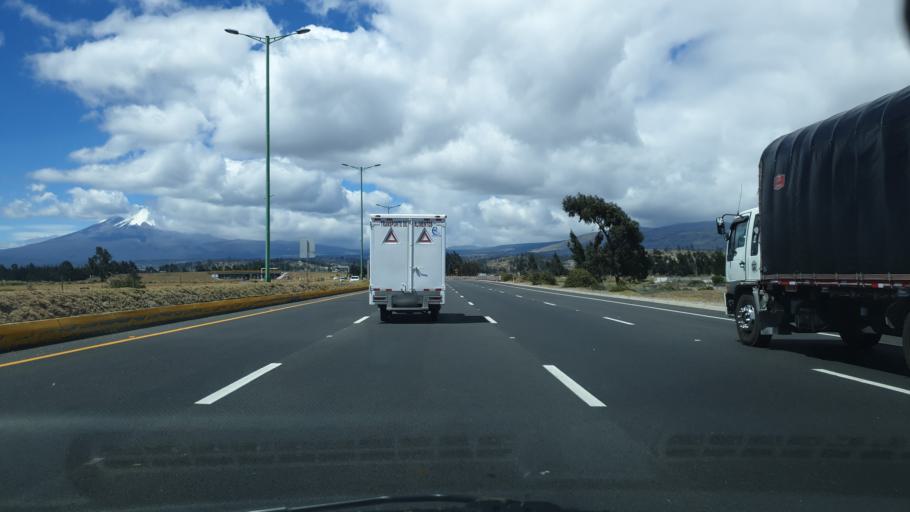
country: EC
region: Cotopaxi
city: Saquisili
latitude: -0.8687
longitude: -78.6319
